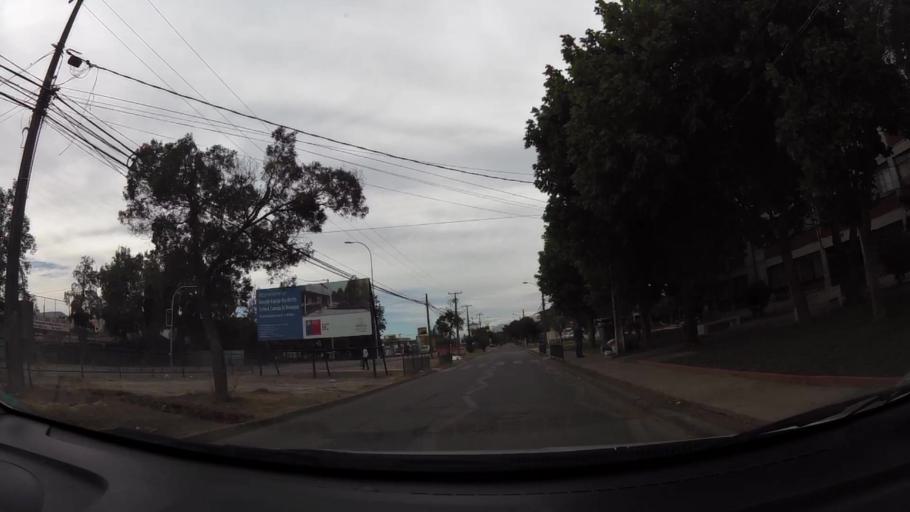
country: CL
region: O'Higgins
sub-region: Provincia de Cachapoal
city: Rancagua
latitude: -34.1468
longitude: -70.7410
